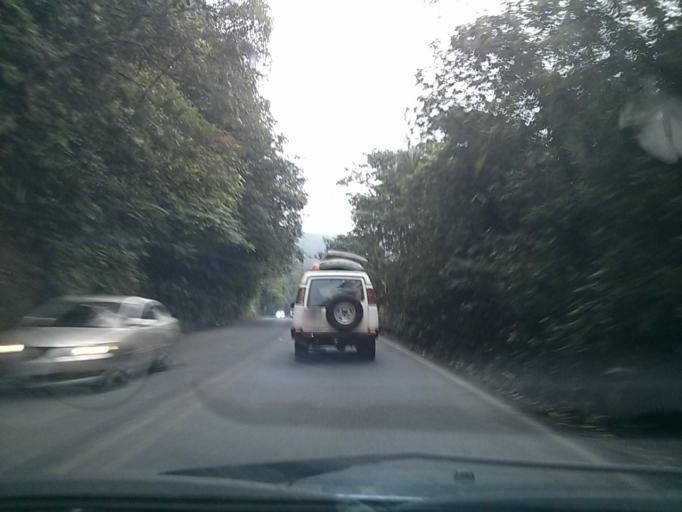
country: CR
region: San Jose
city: Dulce Nombre de Jesus
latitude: 10.1134
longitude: -83.9739
